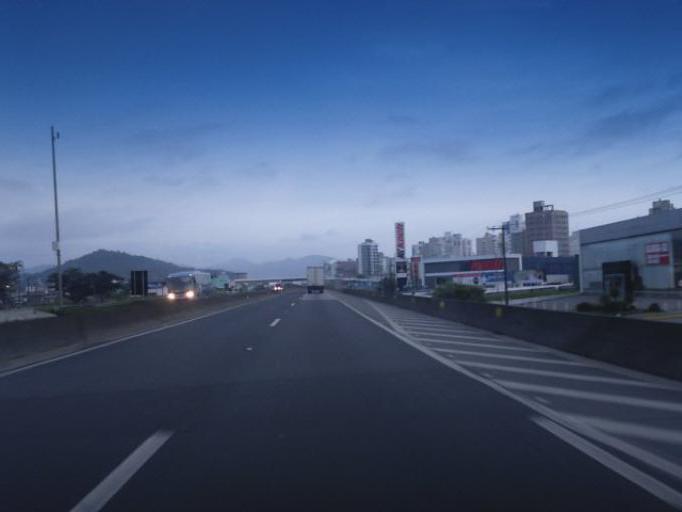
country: BR
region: Santa Catarina
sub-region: Itapema
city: Itapema
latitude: -27.1297
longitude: -48.6096
